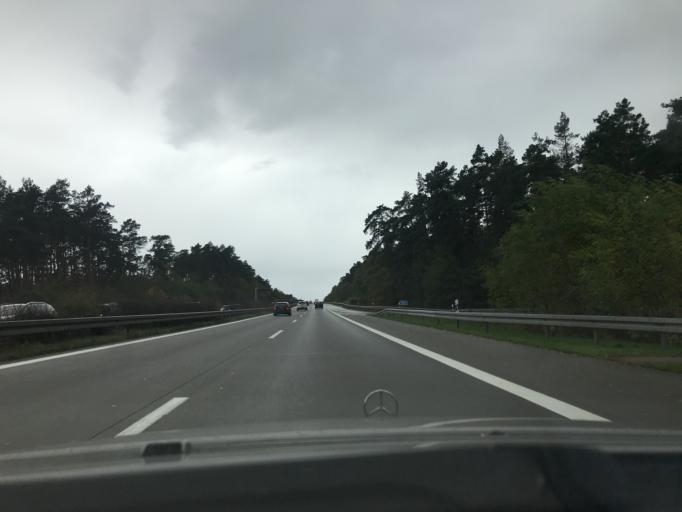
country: DE
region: Brandenburg
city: Marienwerder
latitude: 52.7742
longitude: 13.5653
